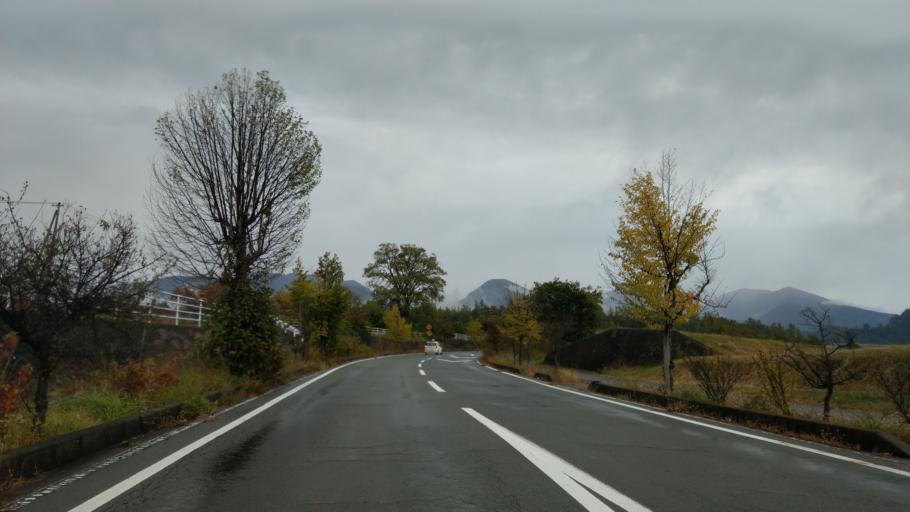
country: JP
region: Nagano
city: Komoro
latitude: 36.3422
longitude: 138.4049
